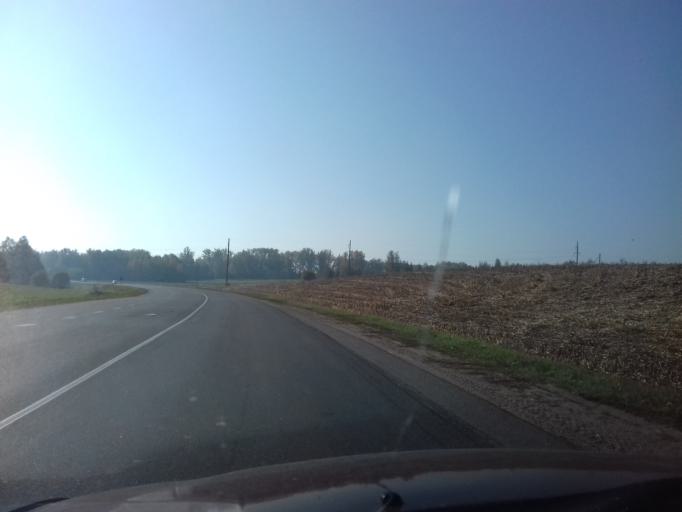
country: BY
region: Minsk
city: Hatava
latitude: 53.7710
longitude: 27.6371
